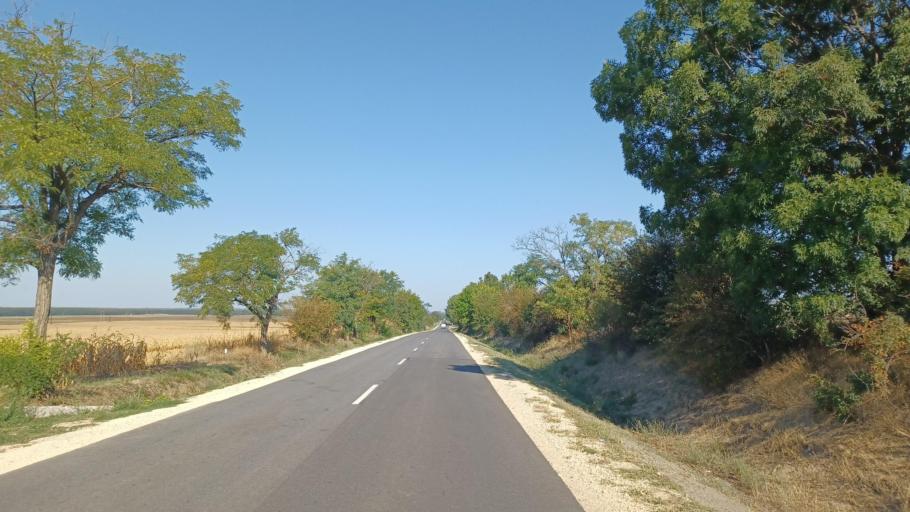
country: HU
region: Tolna
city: Paks
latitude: 46.6525
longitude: 18.8387
